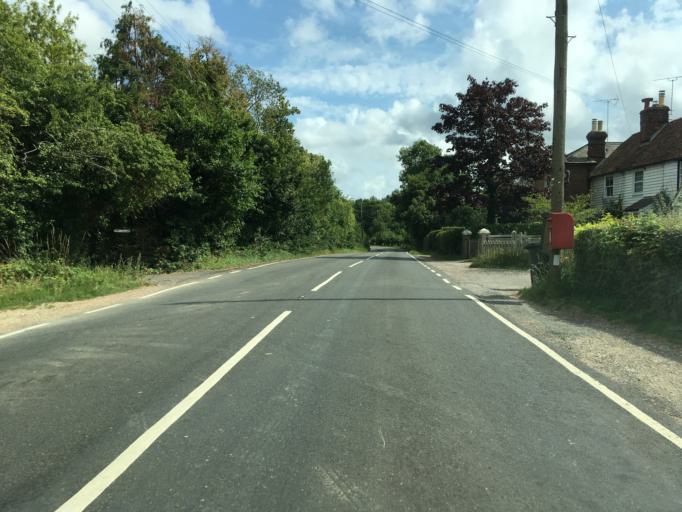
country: GB
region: England
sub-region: Kent
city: Tenterden
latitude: 51.0613
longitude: 0.7168
